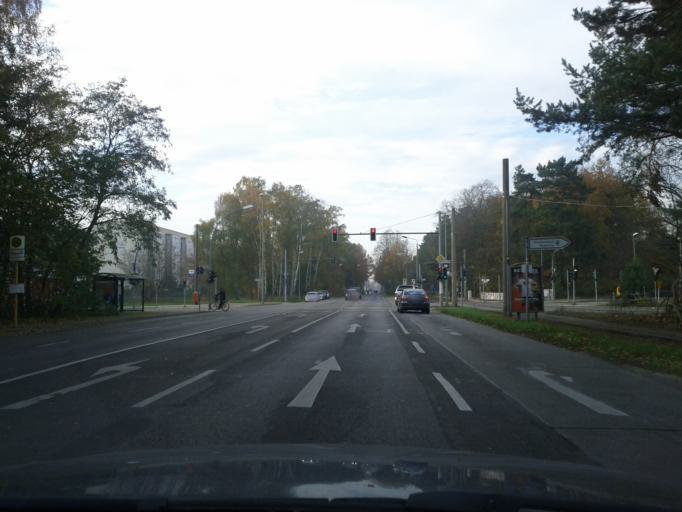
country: DE
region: Berlin
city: Berlin Koepenick
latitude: 52.4383
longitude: 13.5932
